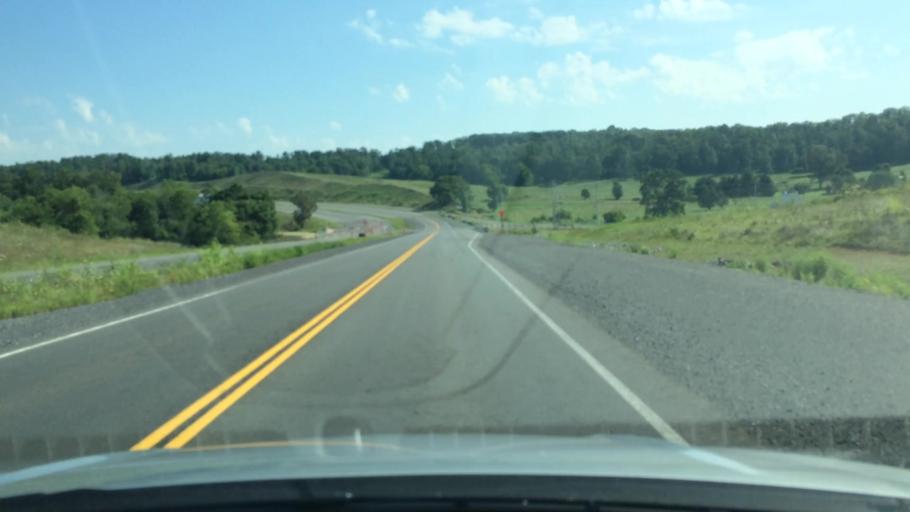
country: US
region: Tennessee
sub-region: Jefferson County
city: White Pine
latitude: 36.1214
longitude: -83.3363
